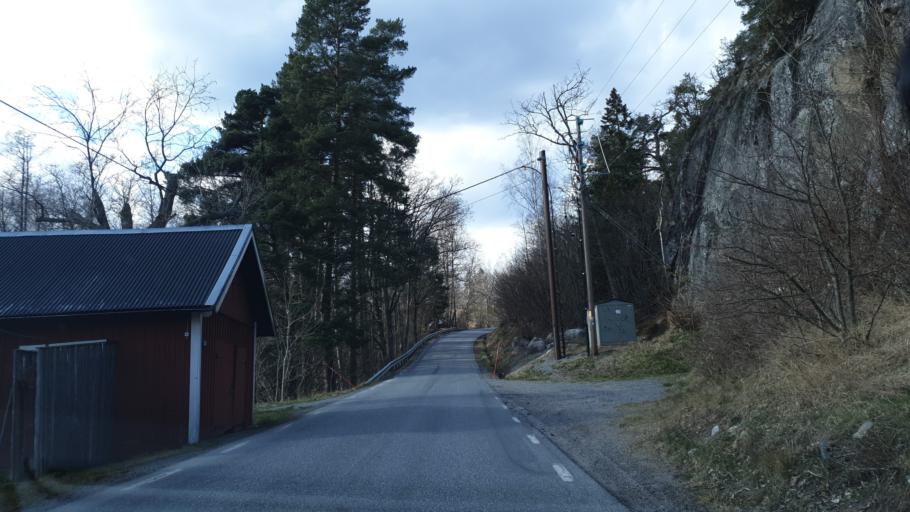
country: SE
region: Stockholm
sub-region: Tyreso Kommun
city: Brevik
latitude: 59.2433
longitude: 18.4448
